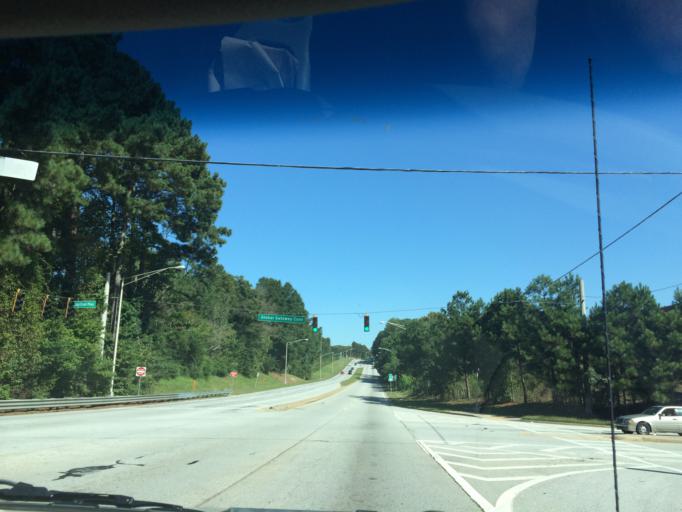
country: US
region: Georgia
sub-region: Fulton County
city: College Park
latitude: 33.6493
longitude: -84.4670
